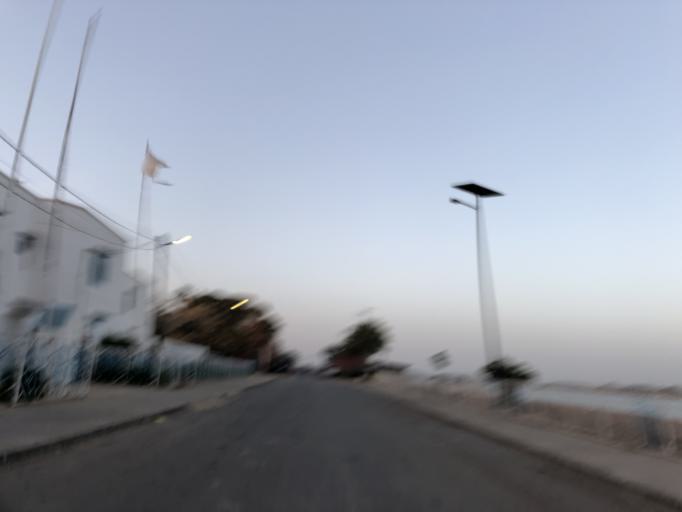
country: SN
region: Saint-Louis
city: Saint-Louis
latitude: 16.0200
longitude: -16.5046
